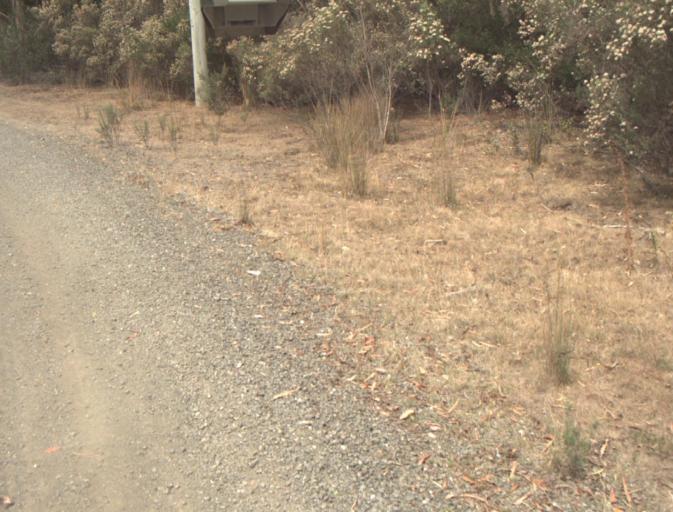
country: AU
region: Tasmania
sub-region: Launceston
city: Mayfield
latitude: -41.1557
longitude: 147.1723
